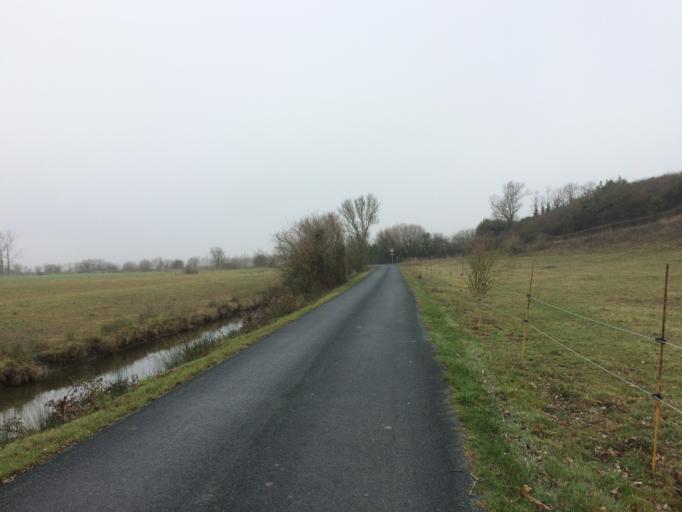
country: FR
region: Pays de la Loire
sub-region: Departement de la Vendee
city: Chaille-les-Marais
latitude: 46.3809
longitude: -1.0258
